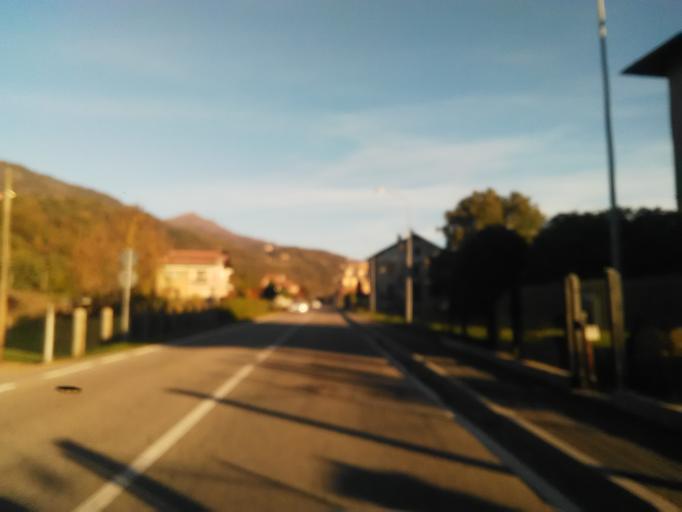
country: IT
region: Piedmont
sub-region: Provincia di Vercelli
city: Borgosesia
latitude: 45.7301
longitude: 8.2635
